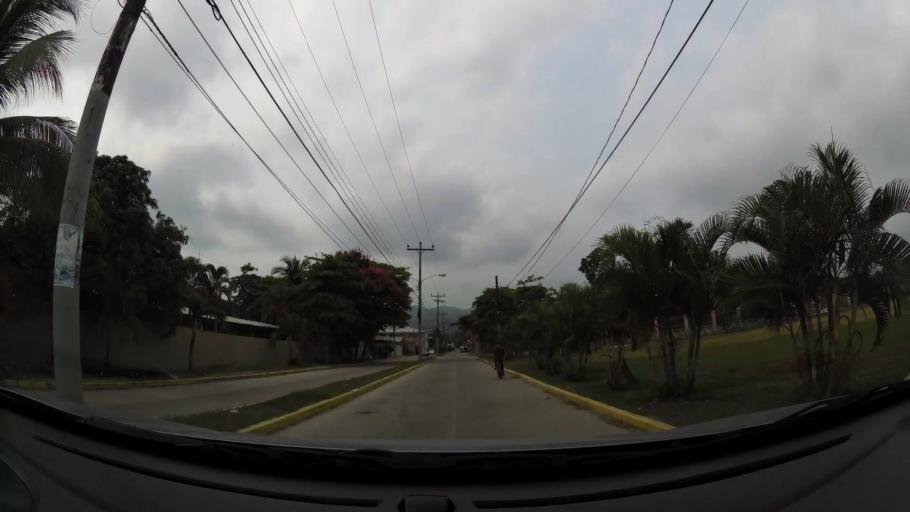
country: HN
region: Atlantida
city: Tela
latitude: 15.7661
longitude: -87.4806
